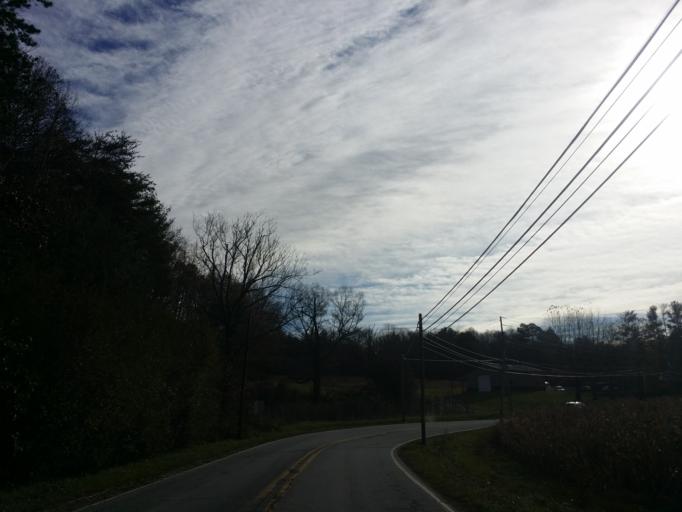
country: US
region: North Carolina
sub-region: Buncombe County
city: Swannanoa
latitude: 35.6118
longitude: -82.4165
